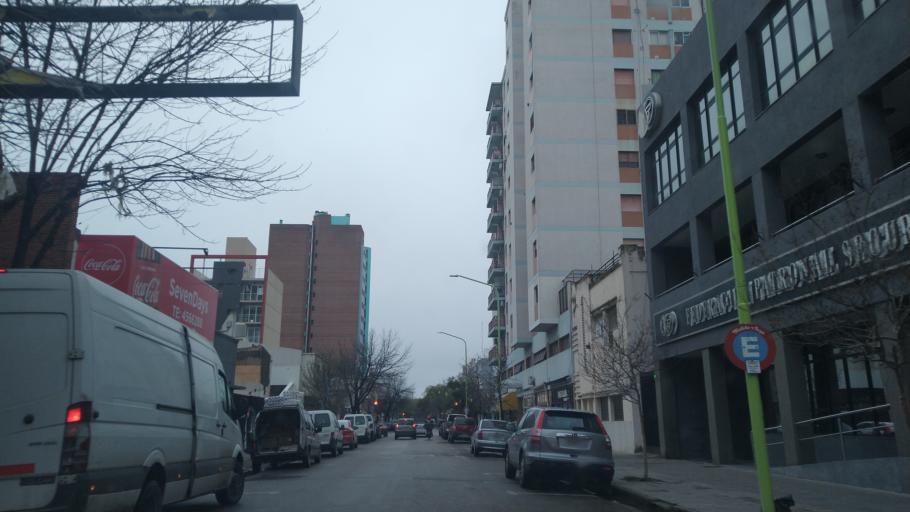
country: AR
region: Buenos Aires
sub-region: Partido de Bahia Blanca
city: Bahia Blanca
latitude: -38.7132
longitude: -62.2685
